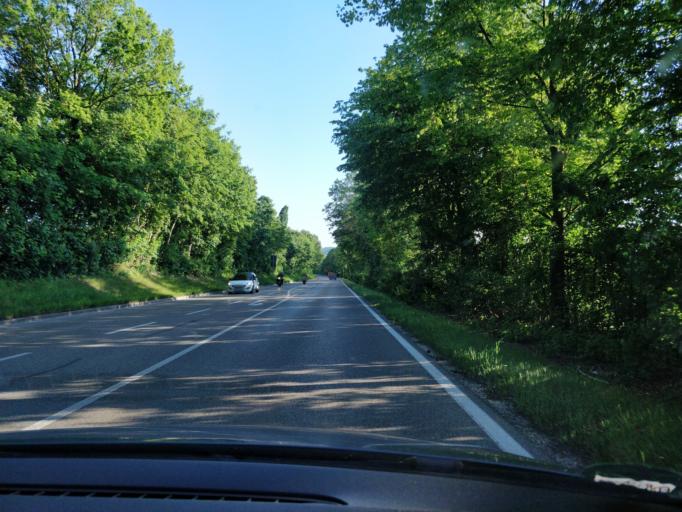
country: DE
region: Bavaria
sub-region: Swabia
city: Noerdlingen
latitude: 48.8441
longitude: 10.4812
